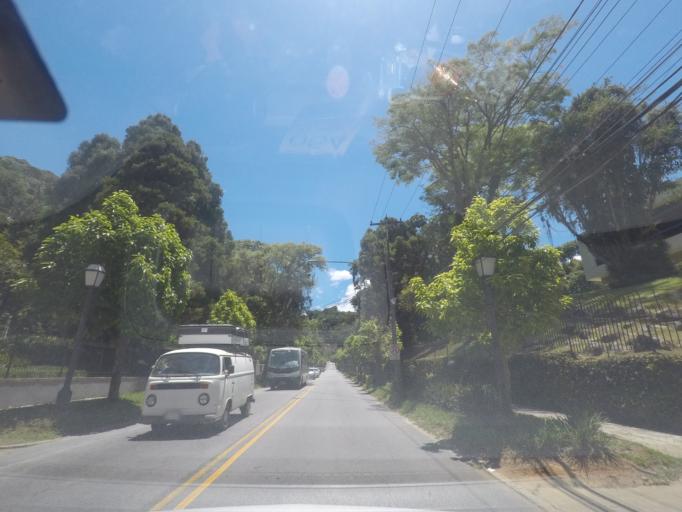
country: BR
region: Rio de Janeiro
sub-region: Petropolis
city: Petropolis
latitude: -22.5038
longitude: -43.1744
